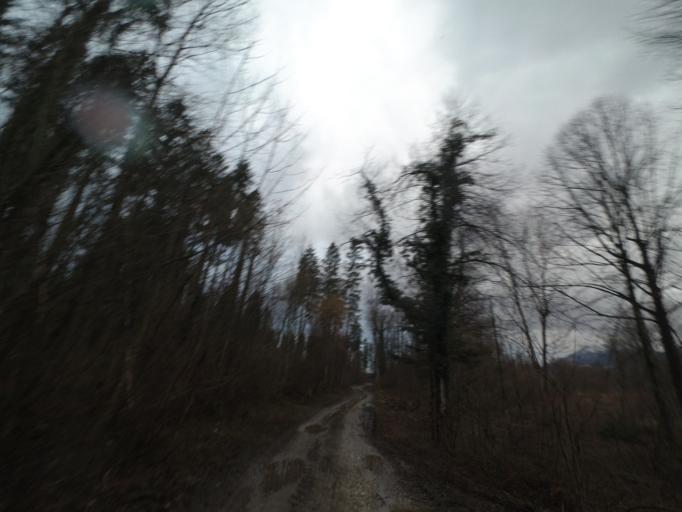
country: AT
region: Salzburg
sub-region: Politischer Bezirk Salzburg-Umgebung
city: Elsbethen
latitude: 47.7400
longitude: 13.0777
